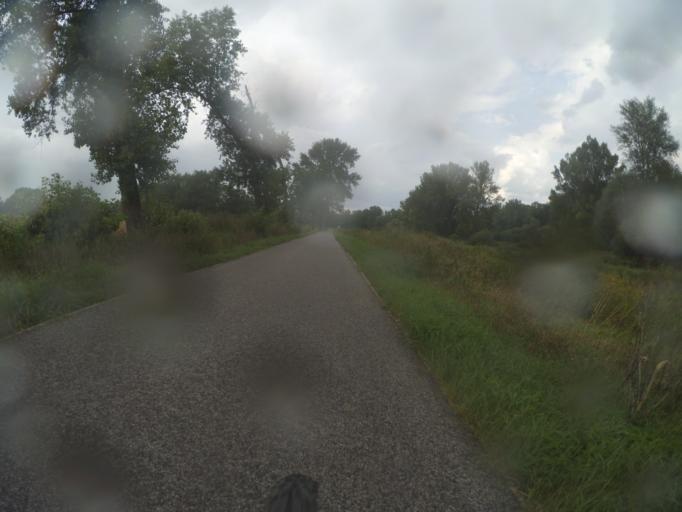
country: CZ
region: Central Bohemia
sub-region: Okres Melnik
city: Melnik
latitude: 50.3340
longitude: 14.4760
